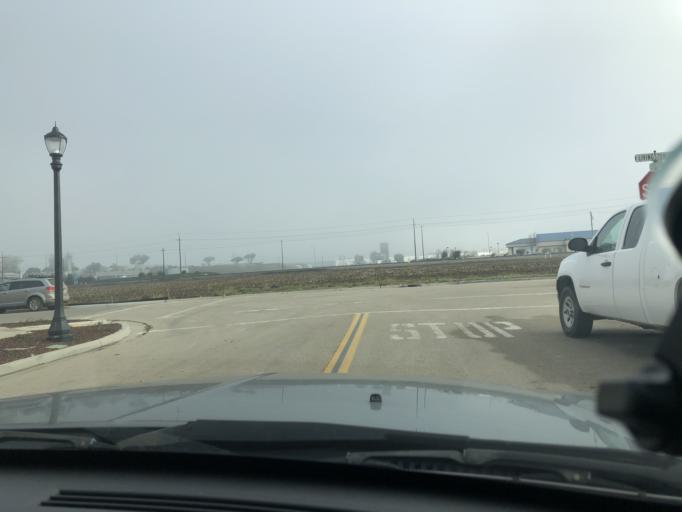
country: US
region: California
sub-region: Monterey County
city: King City
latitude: 36.2218
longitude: -121.1300
